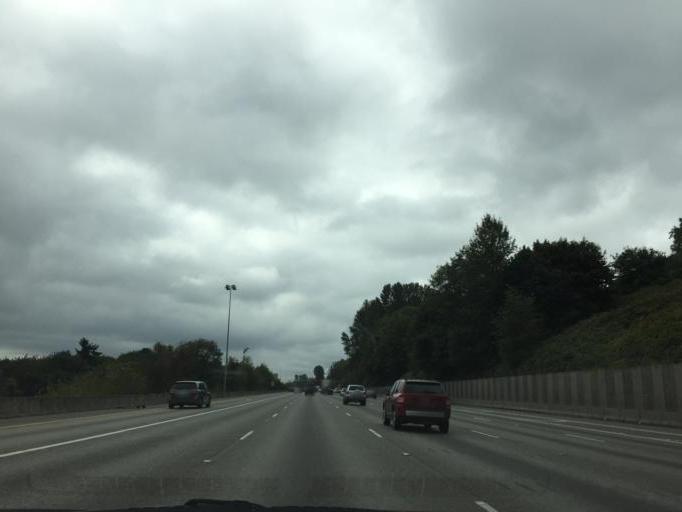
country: US
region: Washington
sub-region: King County
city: Tukwila
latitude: 47.4526
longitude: -122.2651
